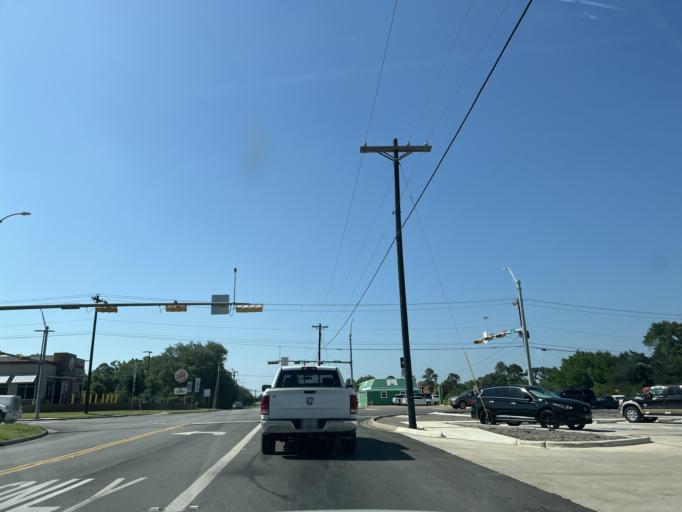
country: US
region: Texas
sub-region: Washington County
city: Brenham
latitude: 30.1760
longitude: -96.4001
